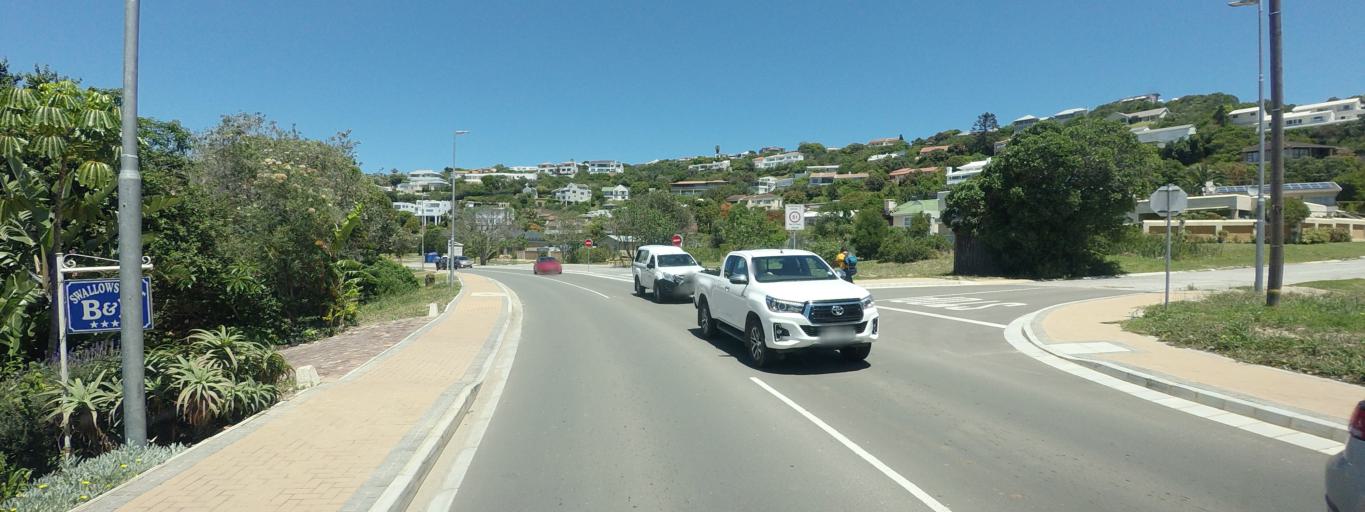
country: ZA
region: Western Cape
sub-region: Eden District Municipality
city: Plettenberg Bay
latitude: -34.0456
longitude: 23.3690
